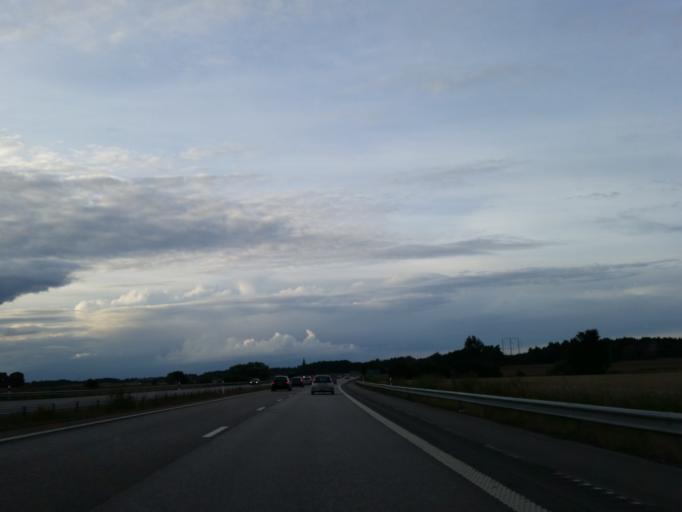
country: SE
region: Uppsala
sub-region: Uppsala Kommun
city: Saevja
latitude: 59.8122
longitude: 17.7563
